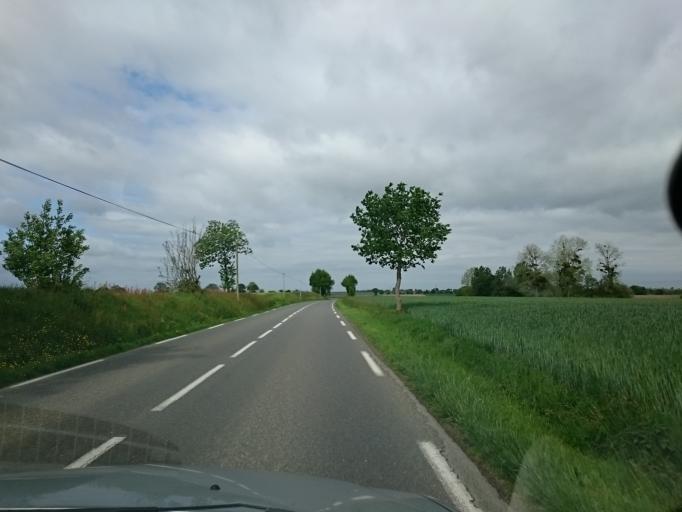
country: FR
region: Lower Normandy
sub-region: Departement de la Manche
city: Saint-James
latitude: 48.5494
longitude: -1.3962
